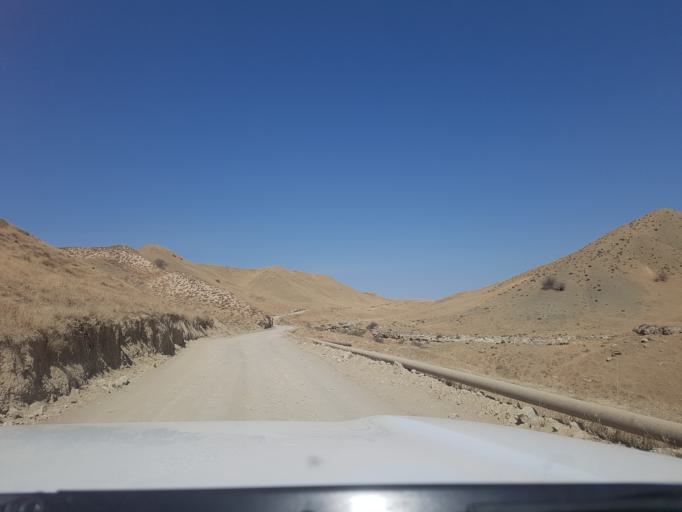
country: TM
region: Ahal
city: Baharly
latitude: 38.2550
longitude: 56.8901
